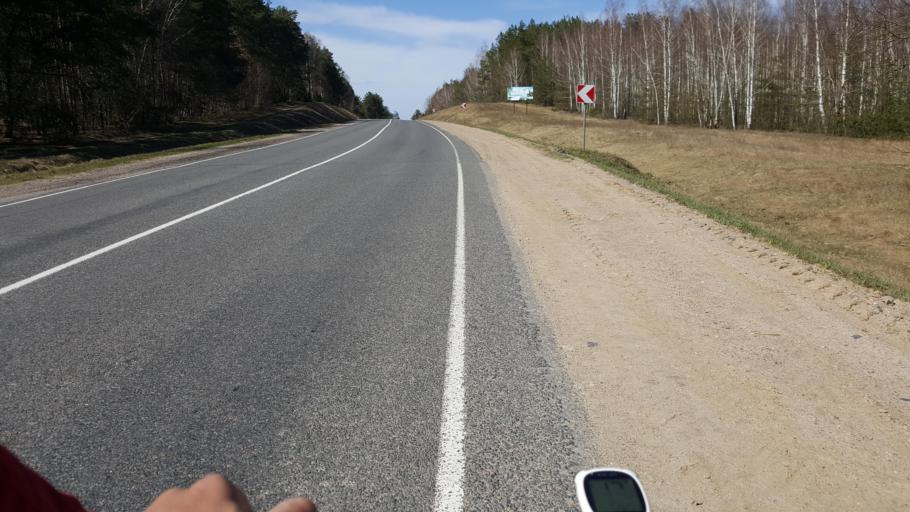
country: BY
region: Brest
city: Kamyanyets
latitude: 52.3439
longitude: 23.7802
